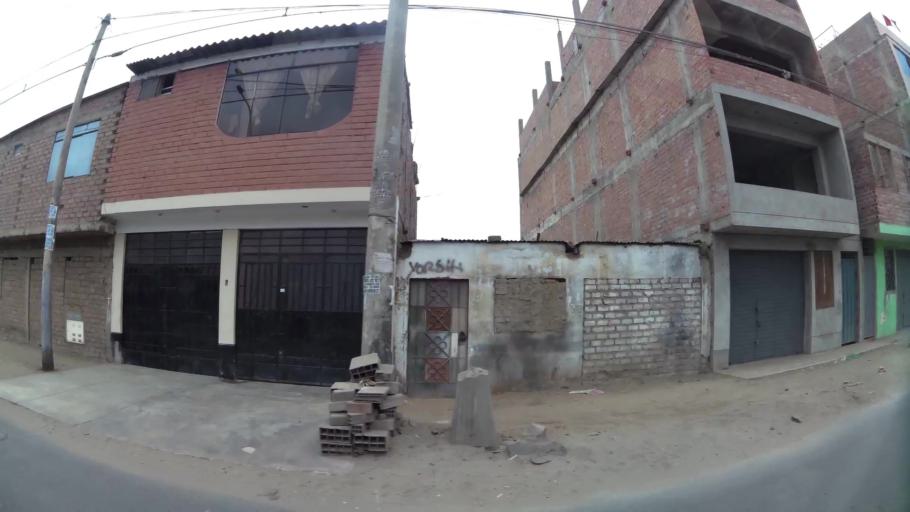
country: PE
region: Lima
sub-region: Lima
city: Surco
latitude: -12.1822
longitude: -76.9660
